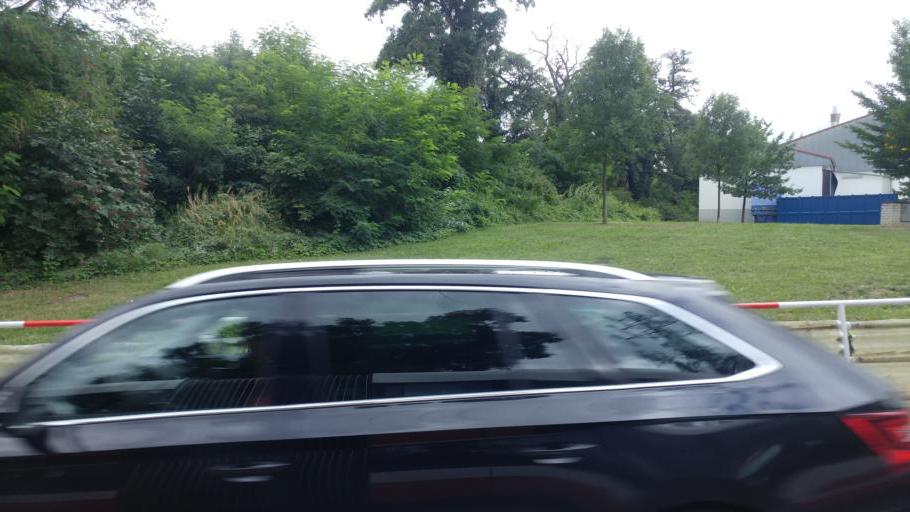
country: CZ
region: Praha
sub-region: Praha 8
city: Liben
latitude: 50.0637
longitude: 14.4944
